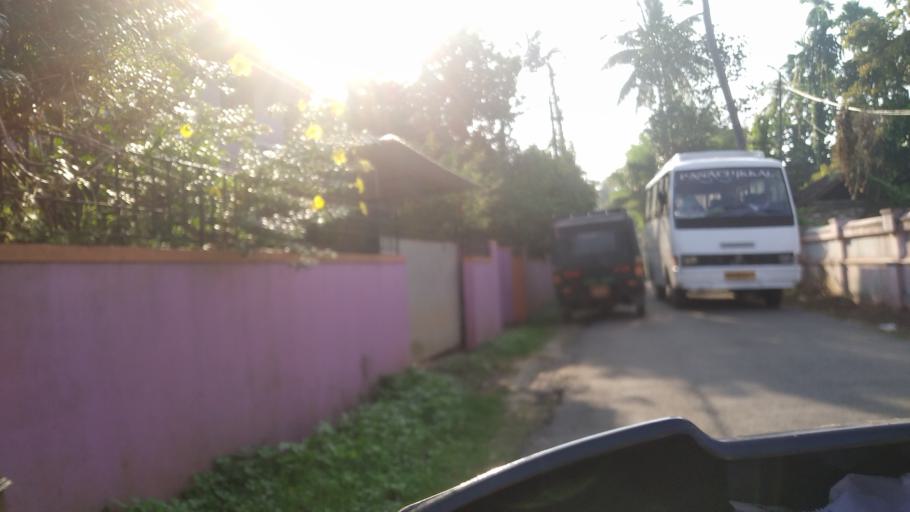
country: IN
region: Kerala
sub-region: Ernakulam
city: Elur
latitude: 10.0462
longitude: 76.2223
